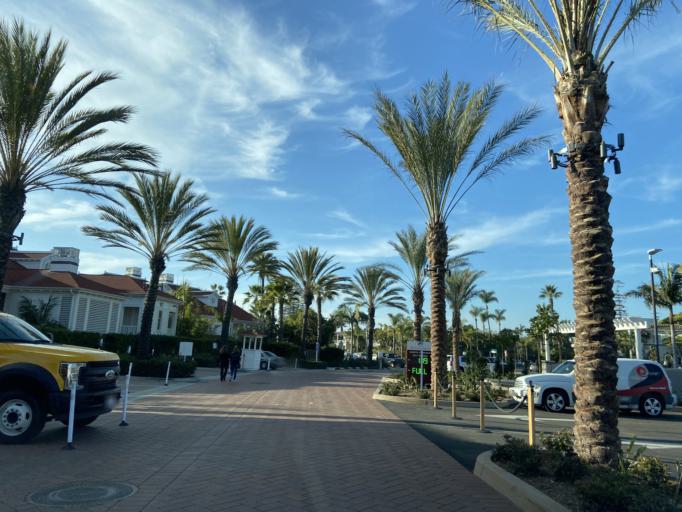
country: US
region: California
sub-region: San Diego County
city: Coronado
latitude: 32.6816
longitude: -117.1795
